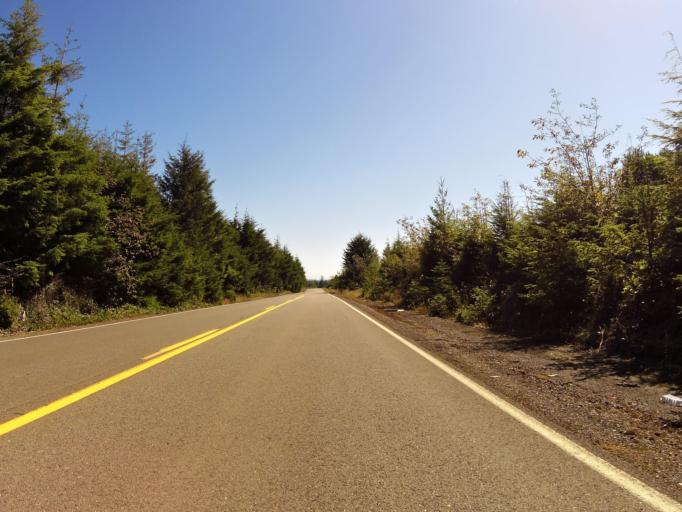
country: US
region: Oregon
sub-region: Coos County
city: Barview
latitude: 43.2612
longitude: -124.3414
